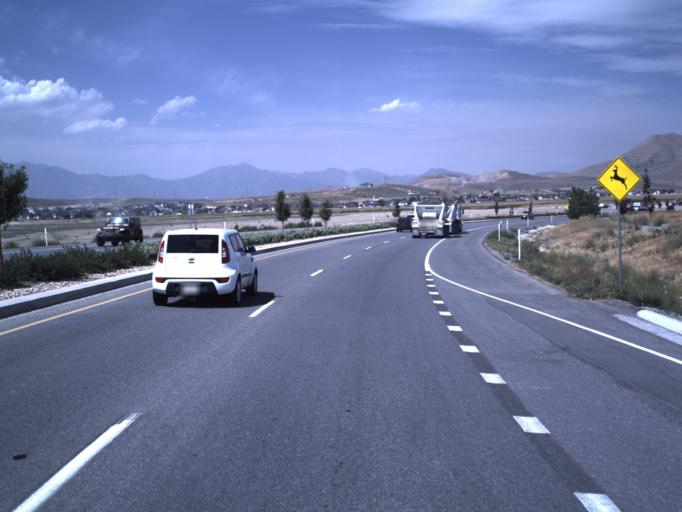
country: US
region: Utah
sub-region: Utah County
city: Saratoga Springs
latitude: 40.3731
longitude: -111.9197
